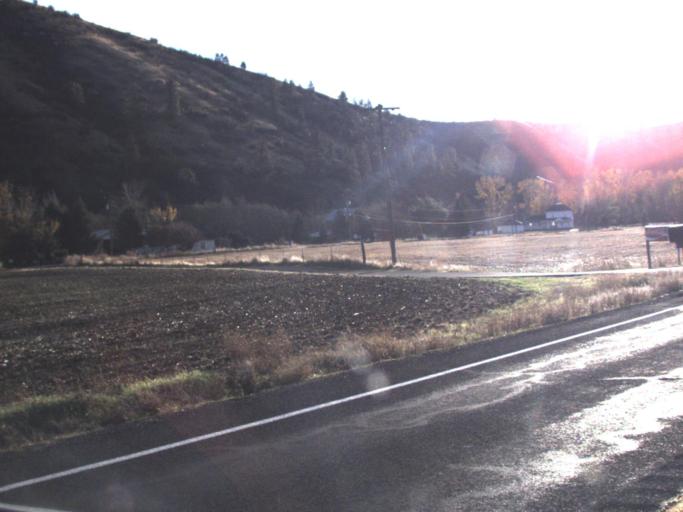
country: US
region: Washington
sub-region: Walla Walla County
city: Waitsburg
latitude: 46.2727
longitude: -118.1270
